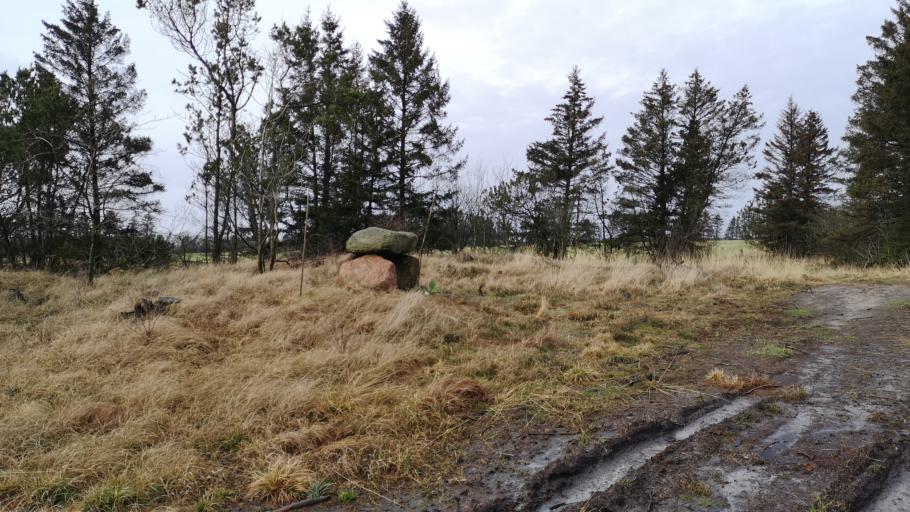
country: DK
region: Central Jutland
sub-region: Ikast-Brande Kommune
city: Brande
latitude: 56.0242
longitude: 9.1456
